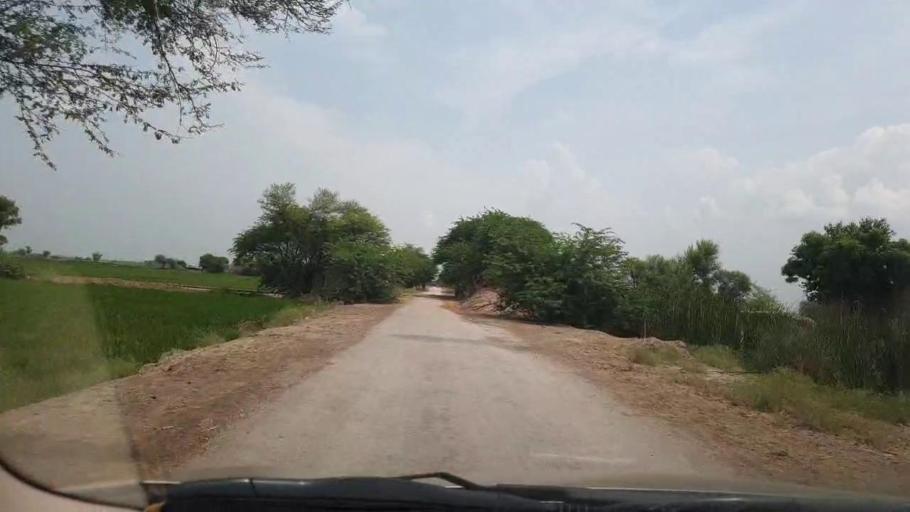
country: PK
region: Sindh
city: Larkana
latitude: 27.6080
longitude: 68.1554
